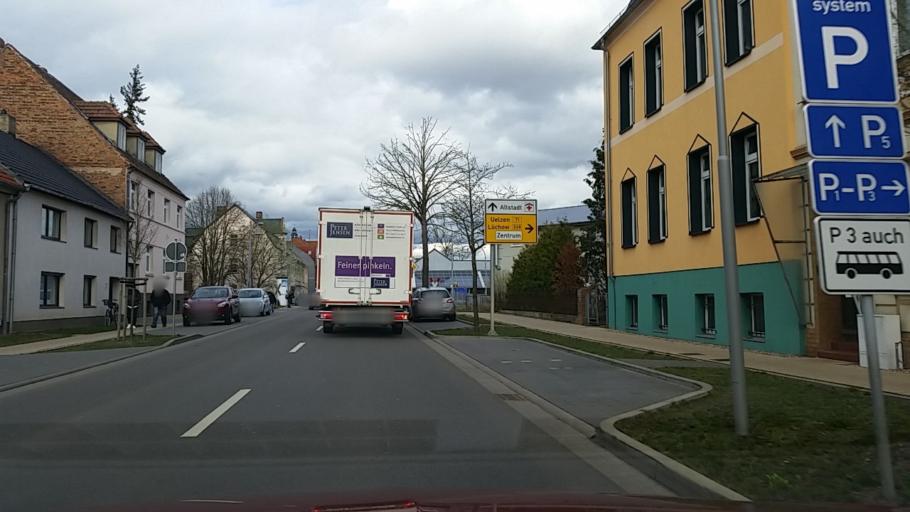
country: DE
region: Saxony-Anhalt
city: Salzwedel
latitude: 52.8432
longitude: 11.1520
